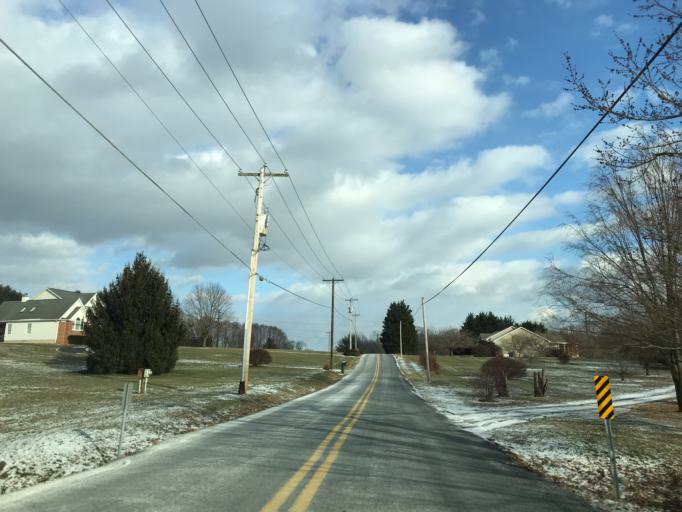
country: US
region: Maryland
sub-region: Harford County
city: Jarrettsville
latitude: 39.6615
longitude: -76.3961
